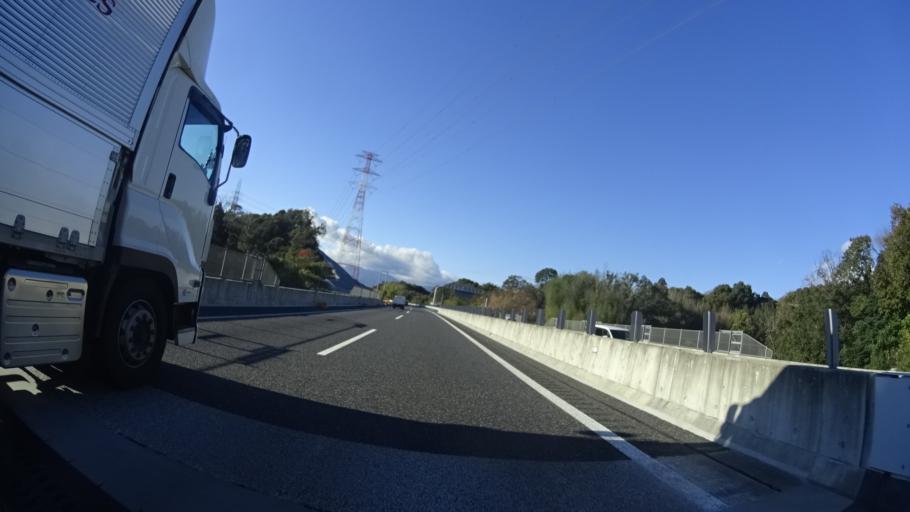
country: JP
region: Mie
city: Yokkaichi
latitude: 35.0448
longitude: 136.6177
